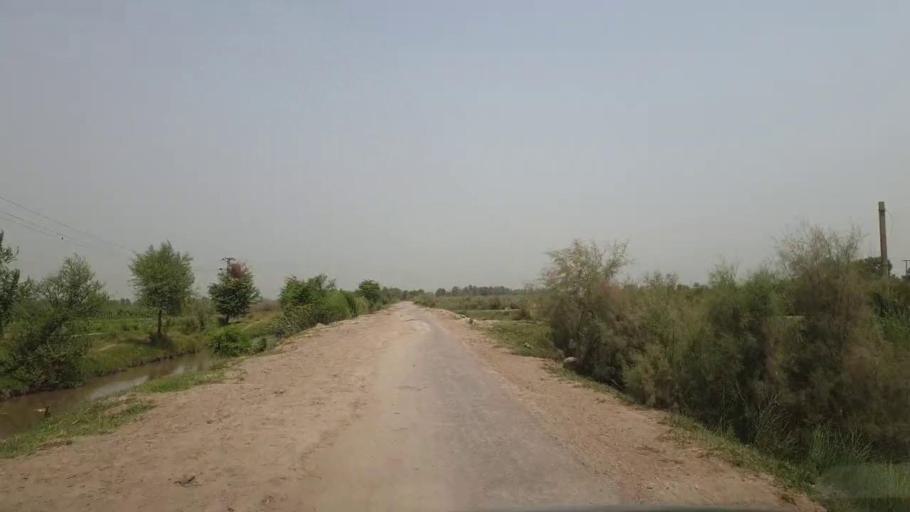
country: PK
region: Sindh
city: Gambat
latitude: 27.4480
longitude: 68.4439
